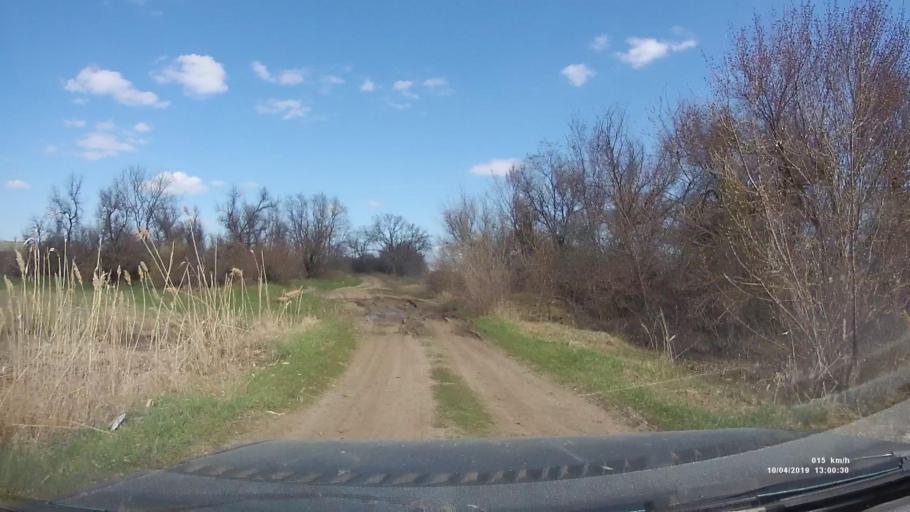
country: RU
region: Rostov
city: Masalovka
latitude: 48.3803
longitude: 40.2299
